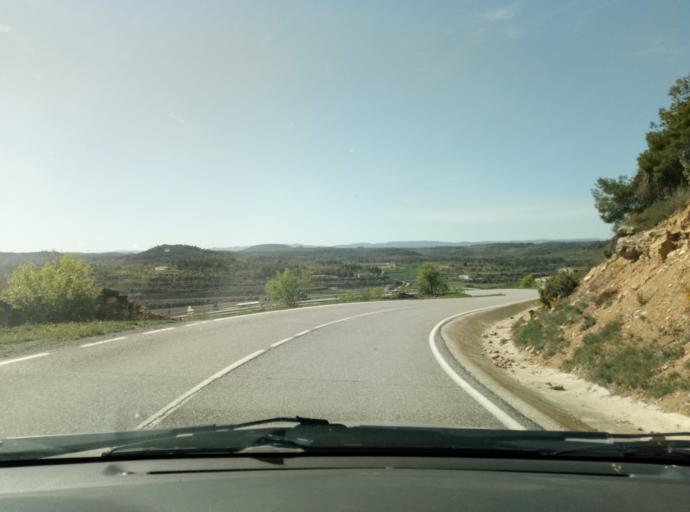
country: ES
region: Catalonia
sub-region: Provincia de Lleida
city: Fulleda
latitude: 41.4991
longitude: 1.0010
